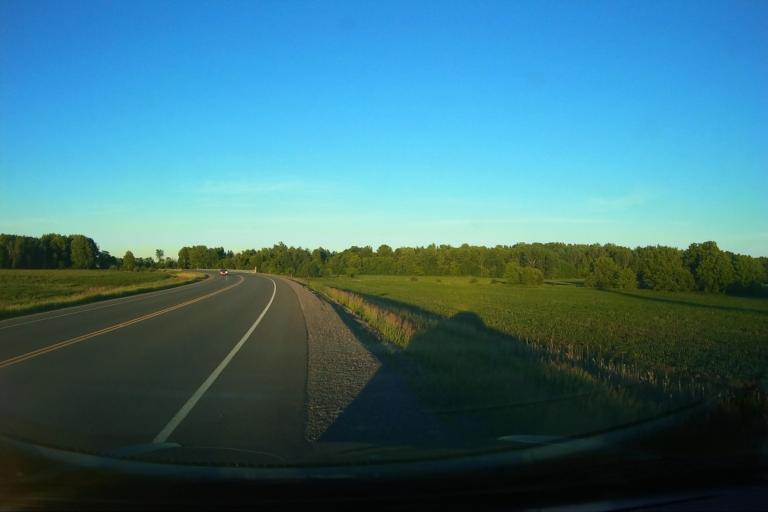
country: CA
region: Ontario
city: Casselman
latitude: 45.0720
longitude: -75.3618
